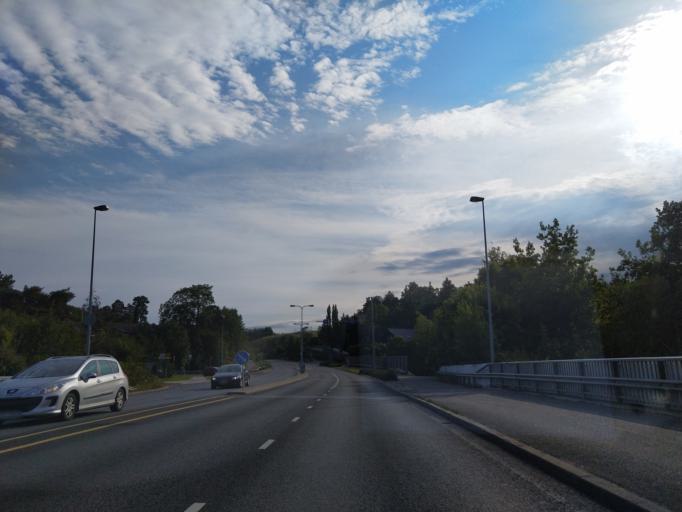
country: FI
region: Varsinais-Suomi
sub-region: Turku
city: Turku
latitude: 60.4218
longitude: 22.2342
